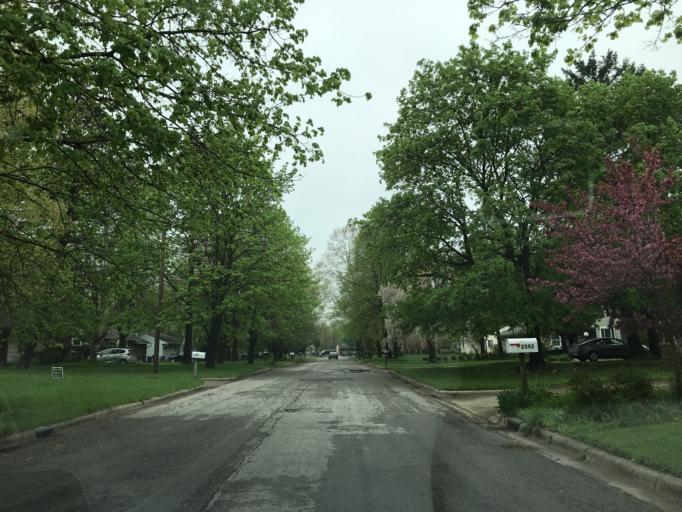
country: US
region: Michigan
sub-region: Washtenaw County
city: Ann Arbor
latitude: 42.2494
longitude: -83.7071
